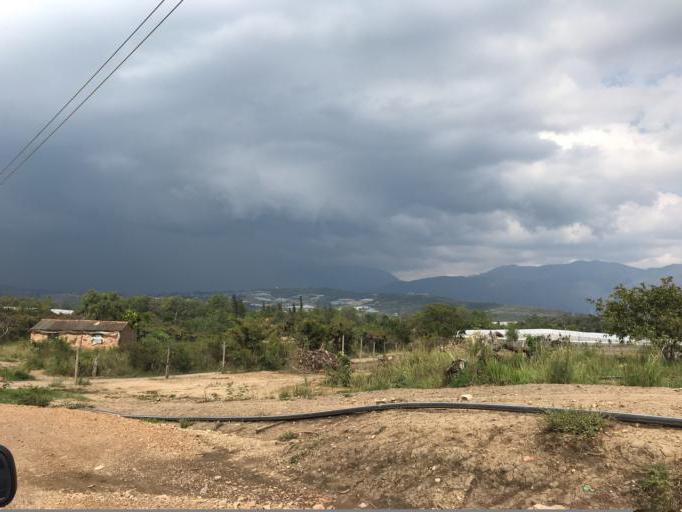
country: CO
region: Boyaca
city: Villa de Leiva
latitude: 5.6542
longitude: -73.5873
